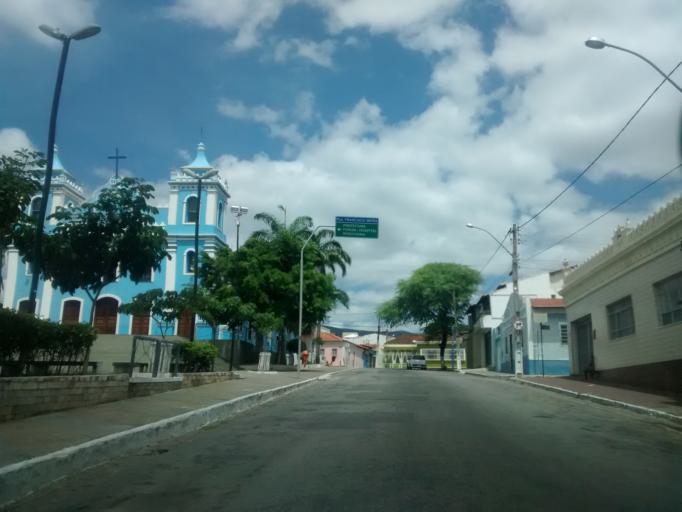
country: BR
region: Bahia
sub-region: Brumado
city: Brumado
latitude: -14.2029
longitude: -41.6640
